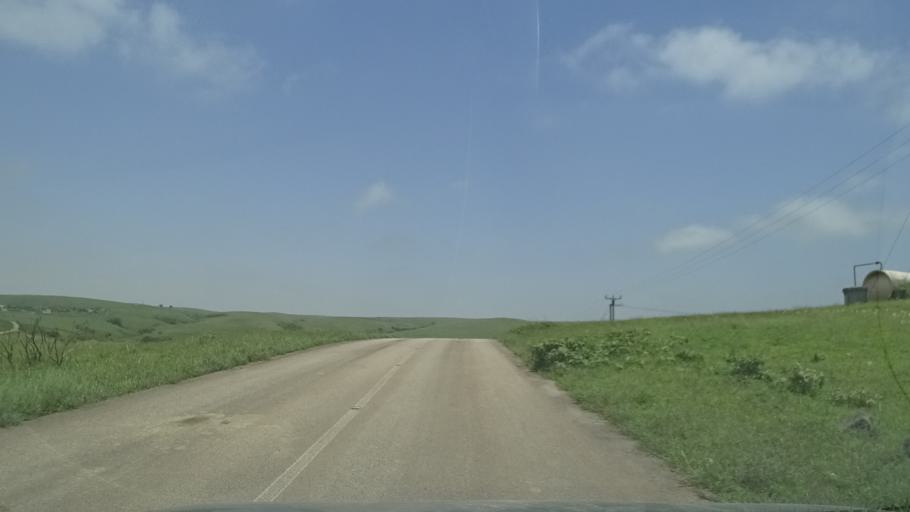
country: OM
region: Zufar
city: Salalah
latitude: 17.2350
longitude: 54.2175
